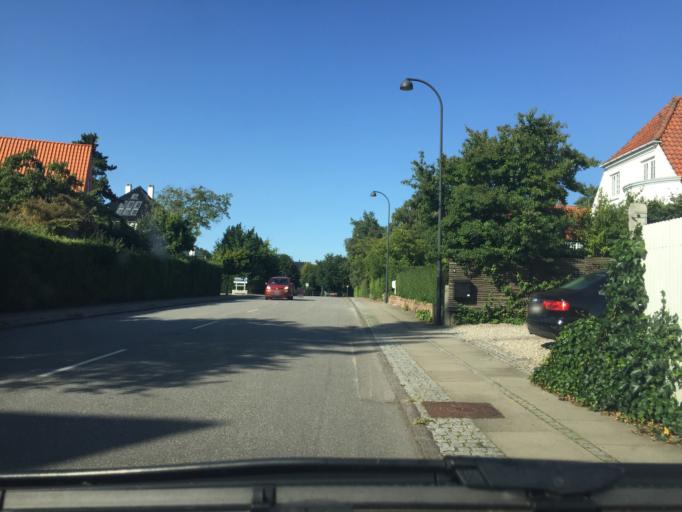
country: DK
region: Capital Region
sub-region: Gentofte Kommune
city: Charlottenlund
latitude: 55.7482
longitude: 12.5653
